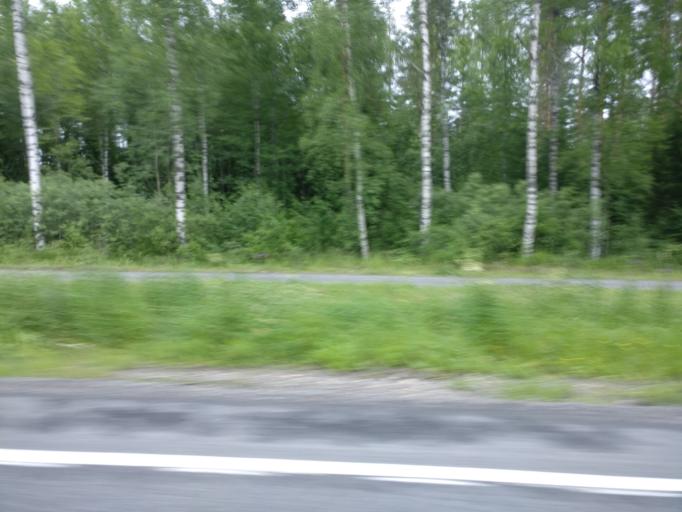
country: FI
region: Northern Savo
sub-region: Varkaus
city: Leppaevirta
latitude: 62.5849
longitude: 27.6053
